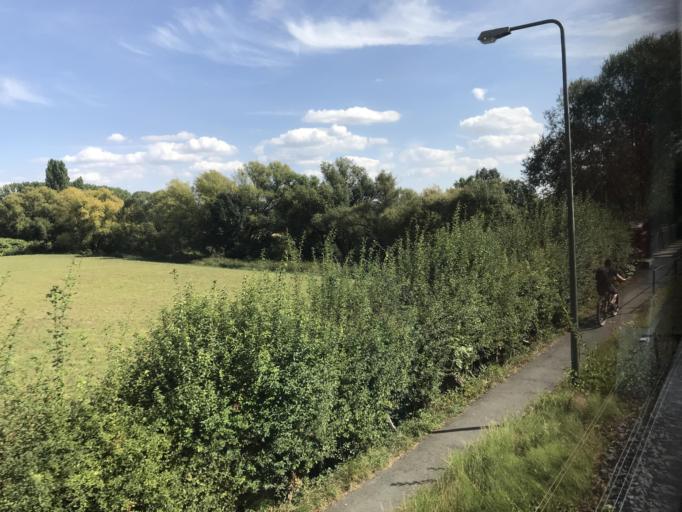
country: DE
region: Hesse
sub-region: Regierungsbezirk Giessen
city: Limburg an der Lahn
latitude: 50.3979
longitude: 8.0473
